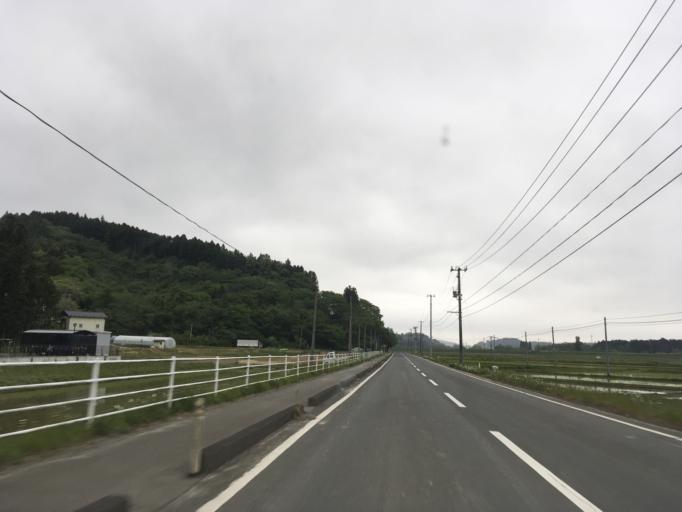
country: JP
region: Miyagi
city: Wakuya
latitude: 38.7261
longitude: 141.2967
